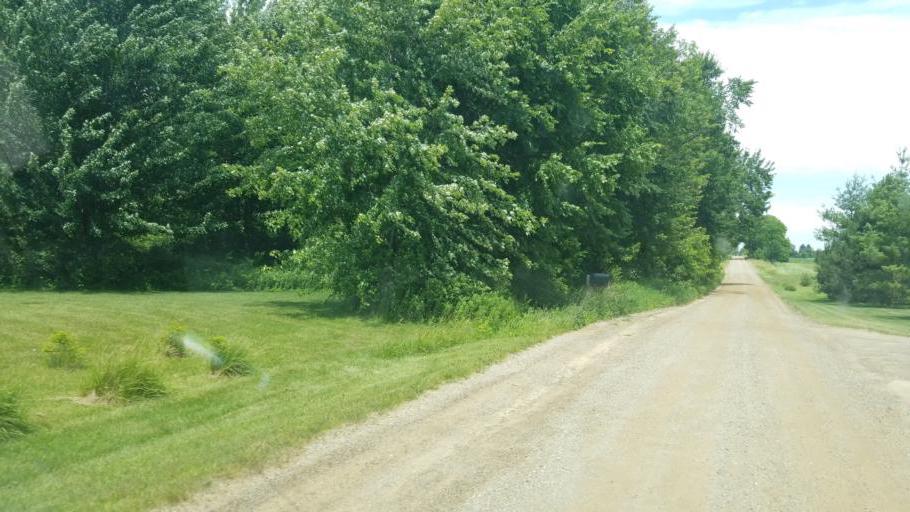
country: US
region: Michigan
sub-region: Eaton County
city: Charlotte
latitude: 42.6485
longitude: -84.9152
